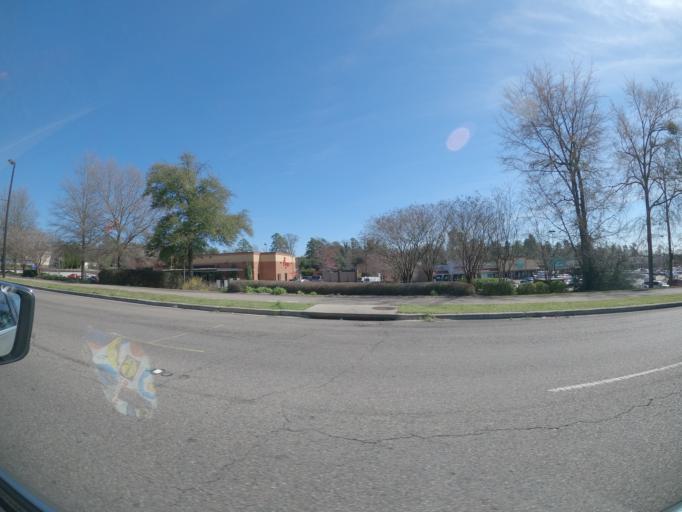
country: US
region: South Carolina
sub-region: Aiken County
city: North Augusta
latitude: 33.5045
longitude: -81.9589
